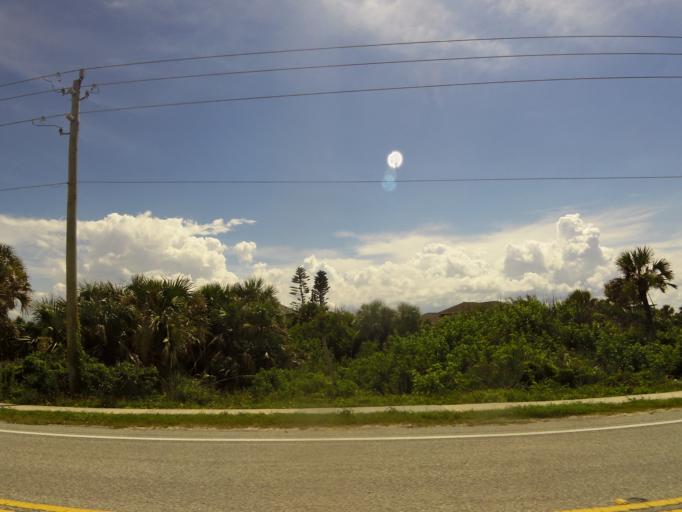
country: US
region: Florida
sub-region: Volusia County
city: Ormond-by-the-Sea
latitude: 29.3852
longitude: -81.0835
